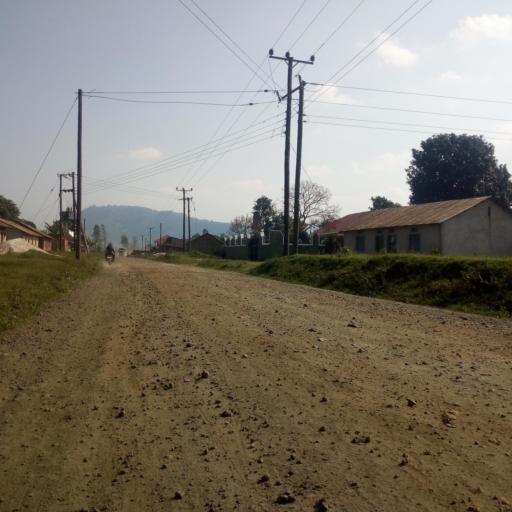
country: UG
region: Western Region
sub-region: Kisoro District
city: Kisoro
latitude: -1.2378
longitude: 29.7134
